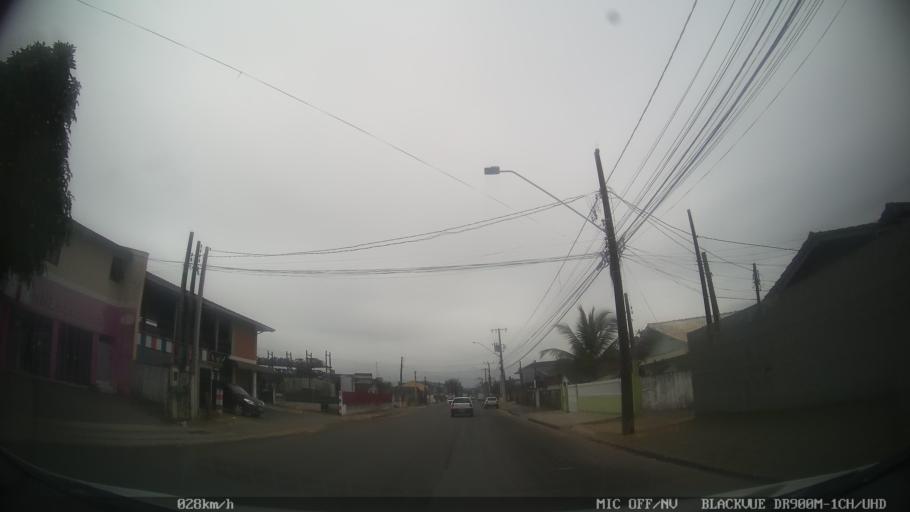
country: BR
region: Santa Catarina
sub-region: Joinville
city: Joinville
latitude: -26.2602
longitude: -48.8093
